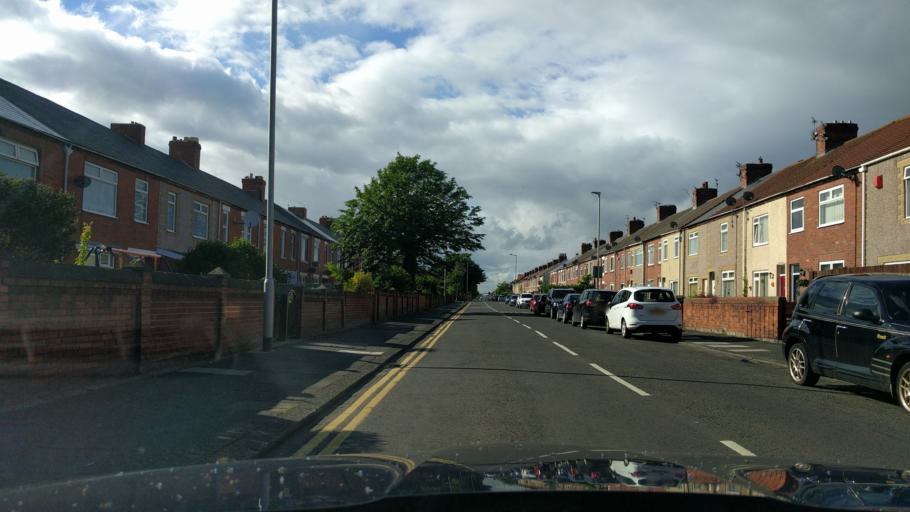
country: GB
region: England
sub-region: Northumberland
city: Ashington
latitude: 55.1774
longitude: -1.5594
